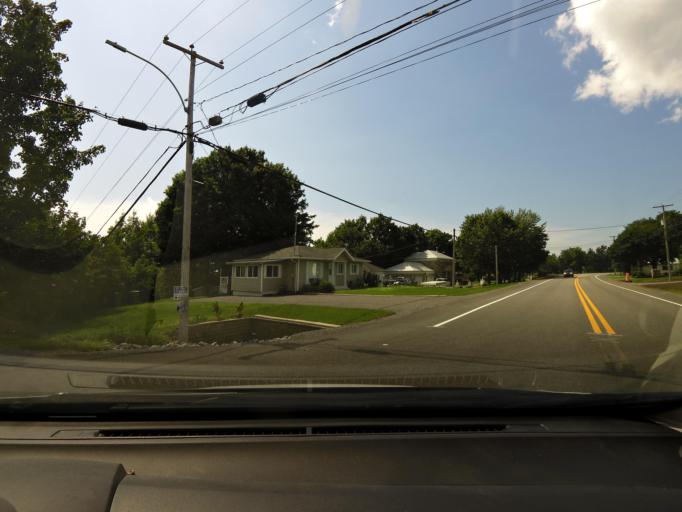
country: CA
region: Quebec
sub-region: Capitale-Nationale
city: Neuville
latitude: 46.7172
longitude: -71.5486
